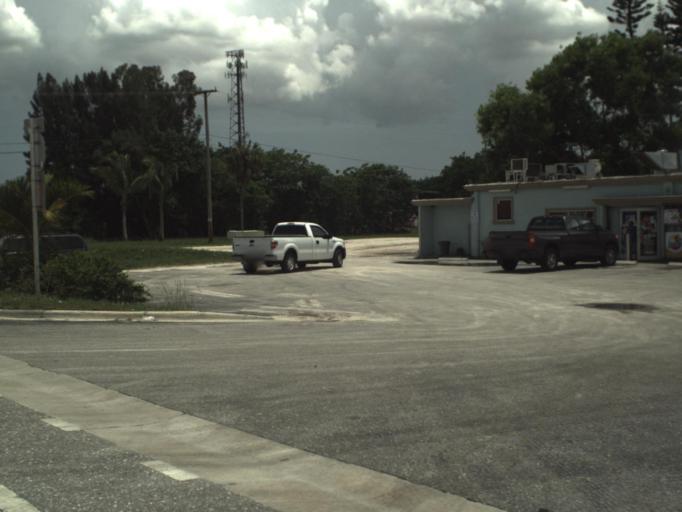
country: US
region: Florida
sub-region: Palm Beach County
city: Villages of Oriole
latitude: 26.5277
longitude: -80.2028
